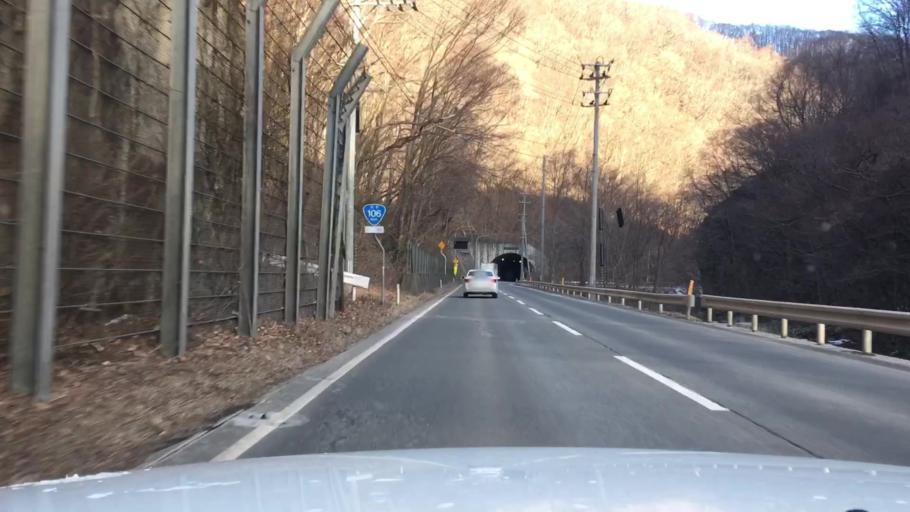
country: JP
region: Iwate
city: Tono
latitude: 39.6389
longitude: 141.5366
